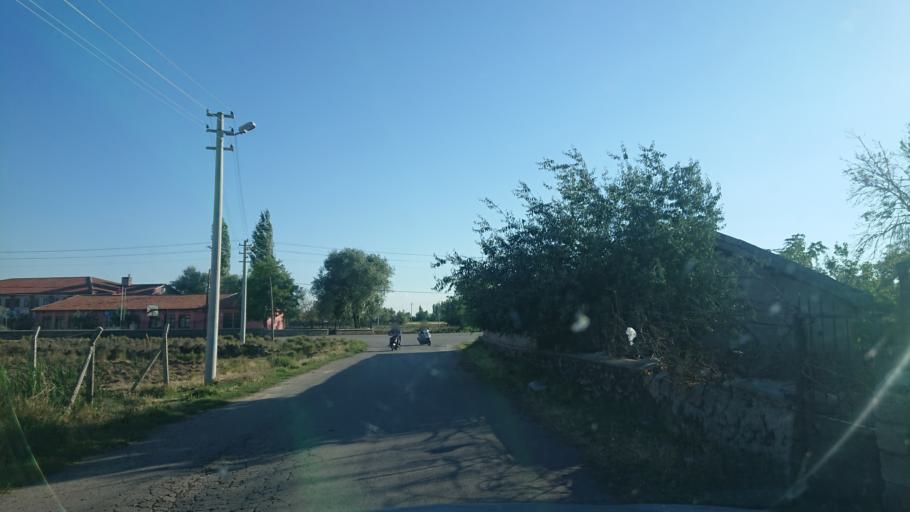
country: TR
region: Aksaray
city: Aksaray
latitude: 38.3858
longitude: 33.9902
